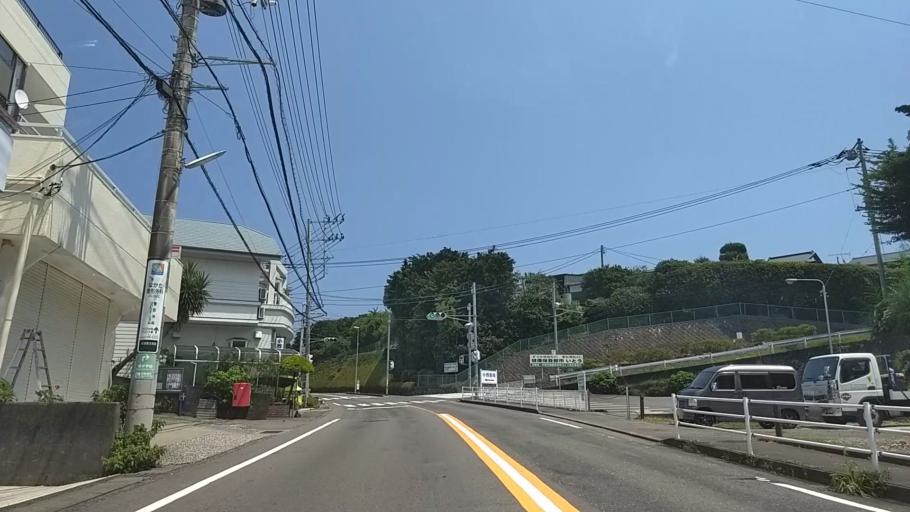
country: JP
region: Shizuoka
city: Ito
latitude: 34.9560
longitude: 139.1098
